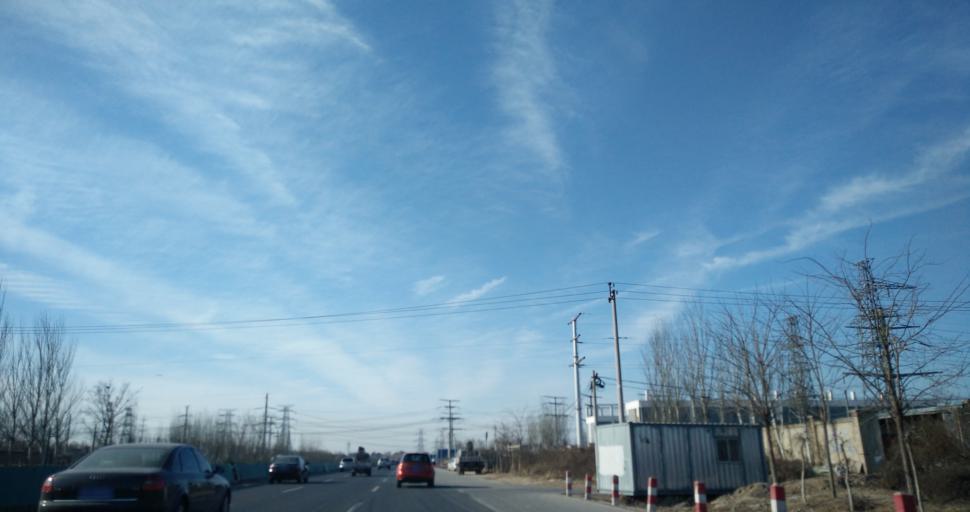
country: CN
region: Beijing
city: Xingfeng
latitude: 39.7421
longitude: 116.3833
